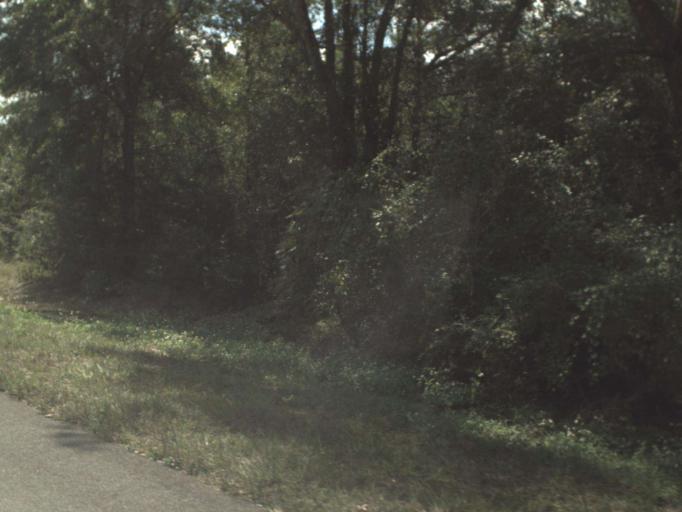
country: US
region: Florida
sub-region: Walton County
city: Freeport
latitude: 30.5579
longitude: -85.9179
